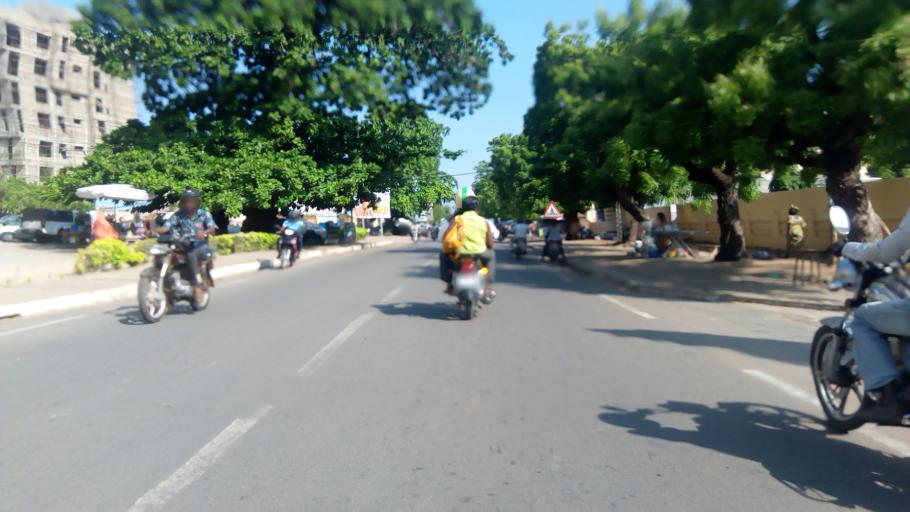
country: TG
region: Maritime
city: Lome
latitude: 6.1336
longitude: 1.2230
